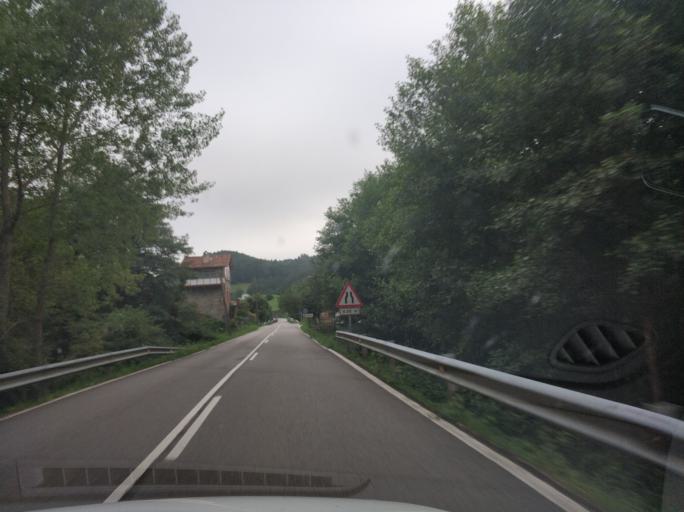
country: ES
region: Asturias
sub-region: Province of Asturias
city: Cudillero
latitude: 43.5528
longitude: -6.1920
